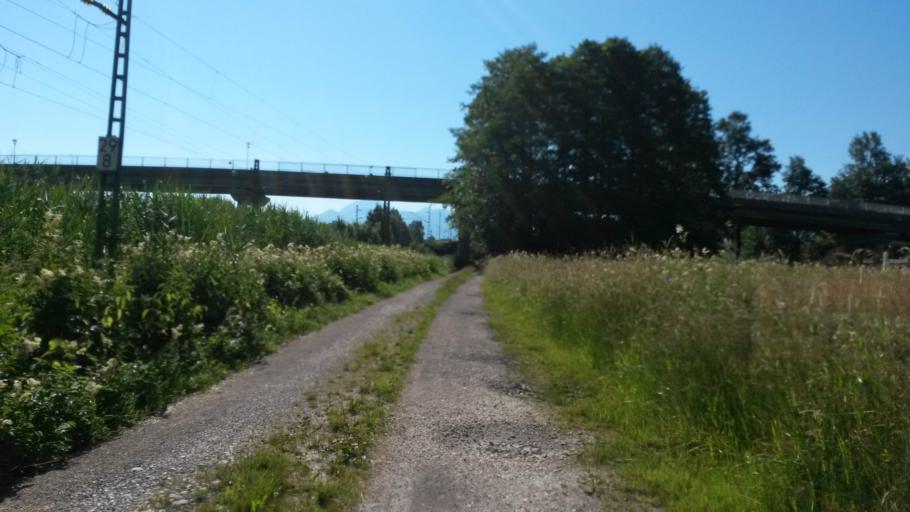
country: DE
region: Bavaria
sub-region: Upper Bavaria
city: Bernau am Chiemsee
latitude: 47.8182
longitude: 12.3767
